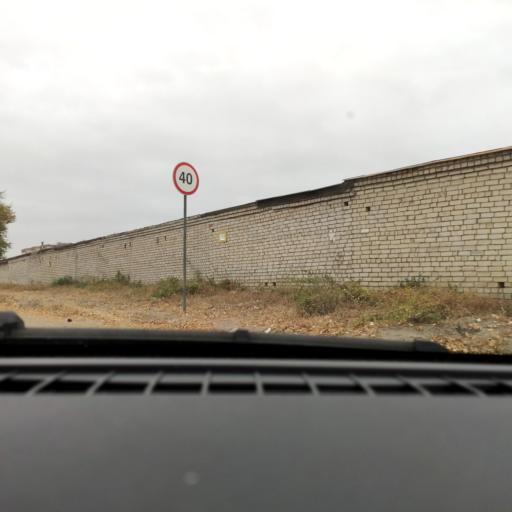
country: RU
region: Voronezj
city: Voronezh
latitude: 51.6620
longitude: 39.2899
